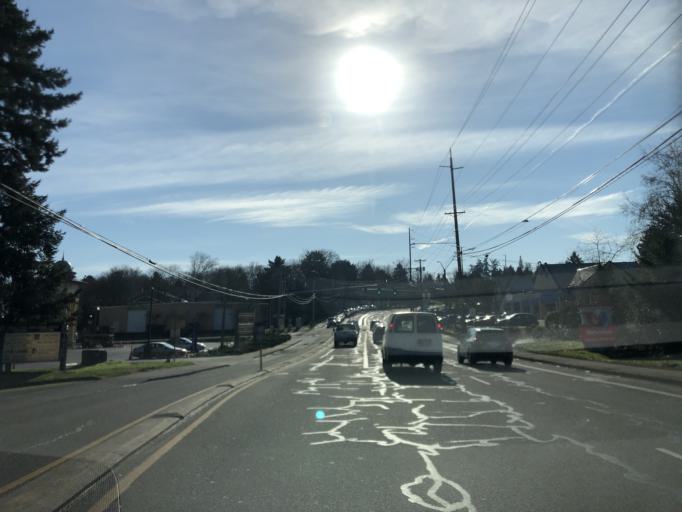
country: US
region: Oregon
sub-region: Washington County
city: Tualatin
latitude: 45.3804
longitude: -122.7644
